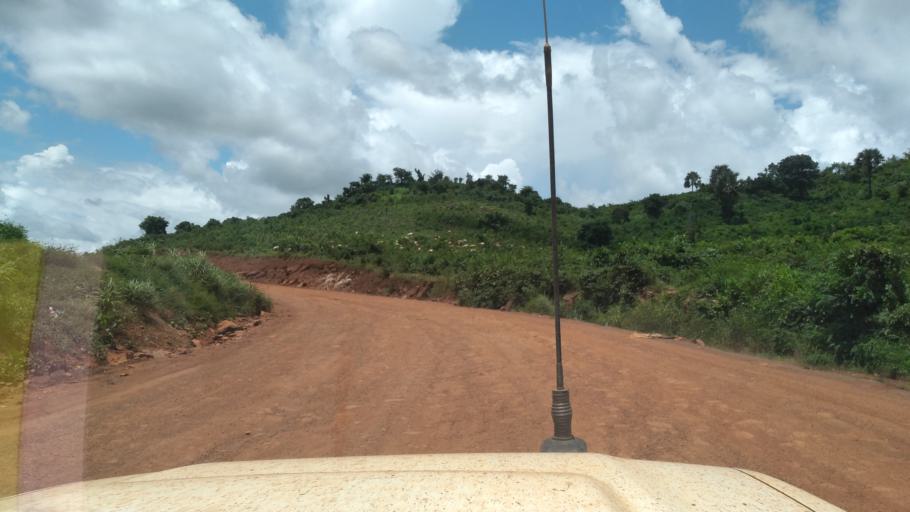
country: GN
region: Mamou
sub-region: Mamou Prefecture
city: Mamou
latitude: 10.2092
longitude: -12.4629
